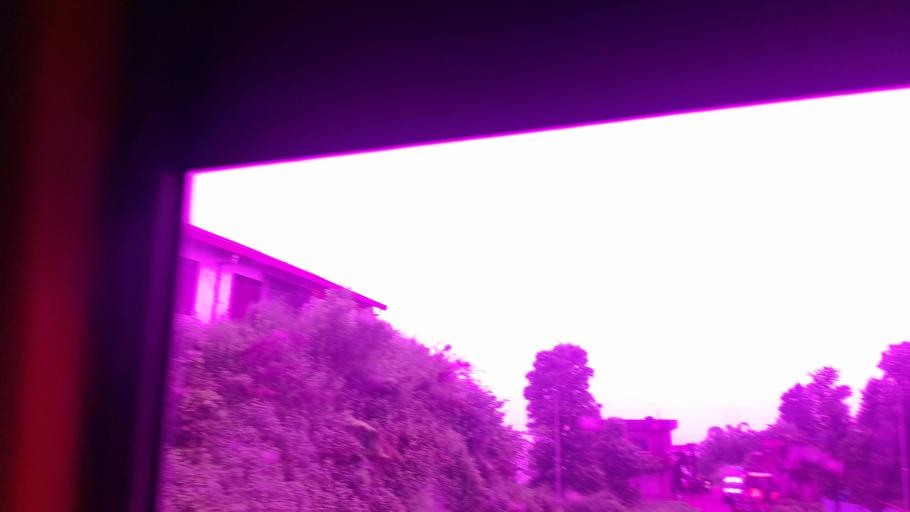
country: NP
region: Central Region
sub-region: Bagmati Zone
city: Kathmandu
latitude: 27.8546
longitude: 85.2247
